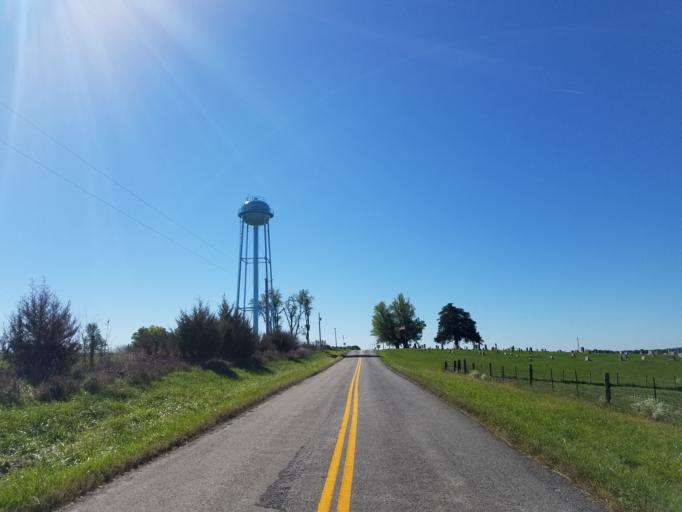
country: US
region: Missouri
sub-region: Mercer County
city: Princeton
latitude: 40.5403
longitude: -93.7179
